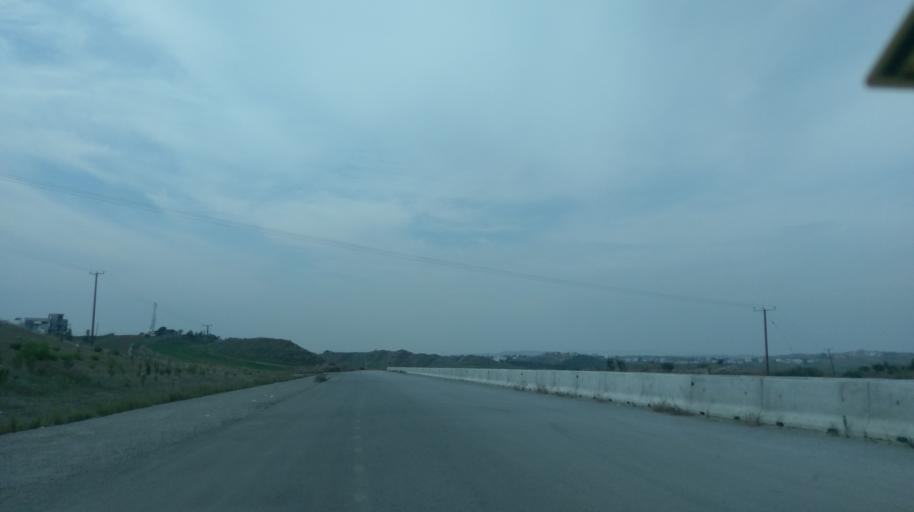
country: CY
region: Lefkosia
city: Nicosia
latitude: 35.2347
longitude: 33.3180
